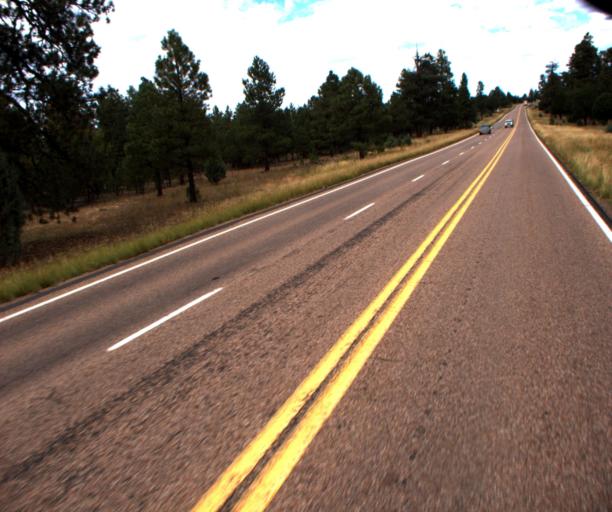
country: US
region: Arizona
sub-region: Navajo County
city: Heber-Overgaard
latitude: 34.3875
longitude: -110.6709
